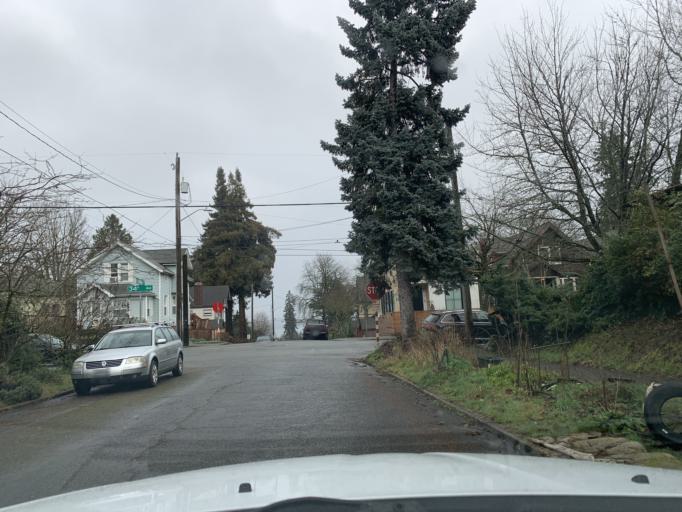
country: US
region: Washington
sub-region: King County
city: Seattle
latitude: 47.6092
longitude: -122.2898
